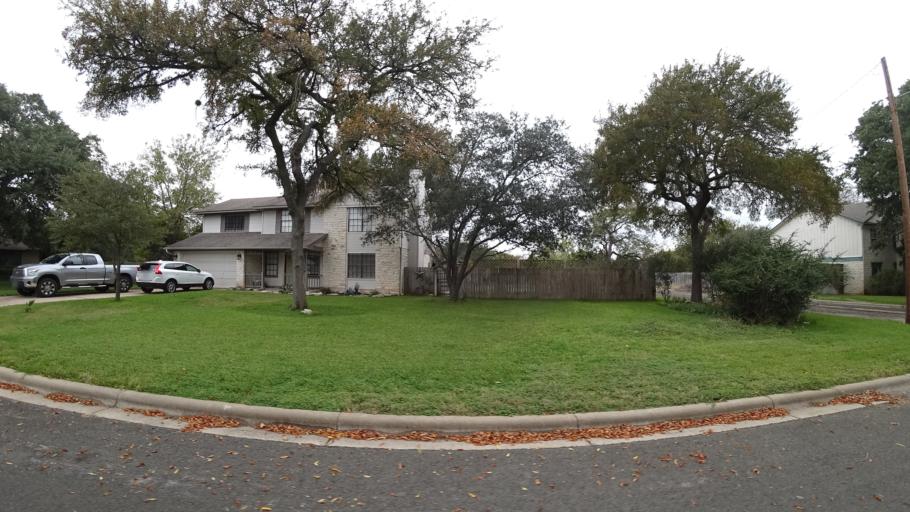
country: US
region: Texas
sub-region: Williamson County
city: Round Rock
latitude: 30.4828
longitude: -97.7041
